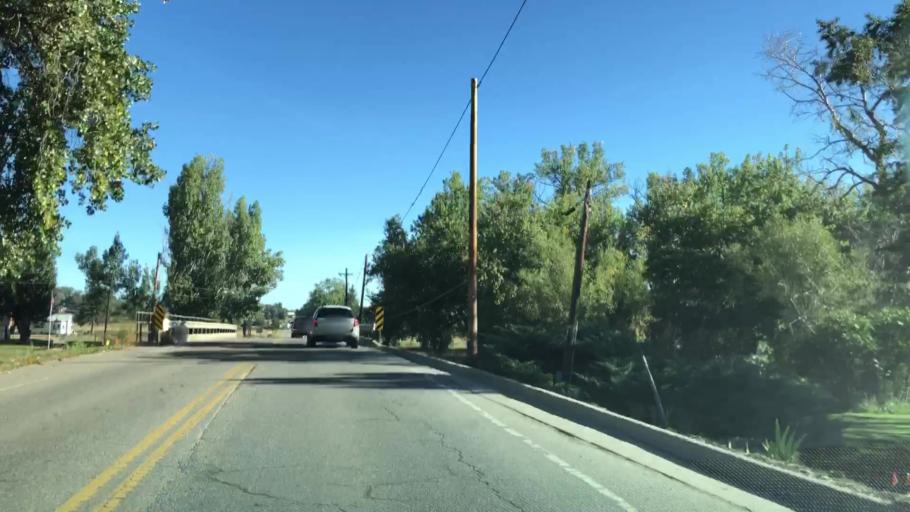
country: US
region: Colorado
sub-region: Larimer County
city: Loveland
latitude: 40.4001
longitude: -105.1233
